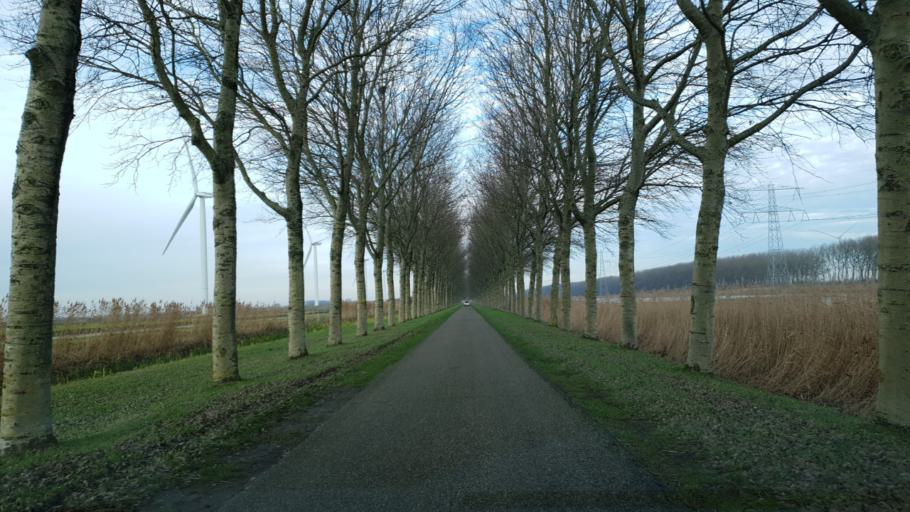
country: NL
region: North Brabant
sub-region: Gemeente Woensdrecht
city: Woensdrecht
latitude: 51.4094
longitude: 4.2334
